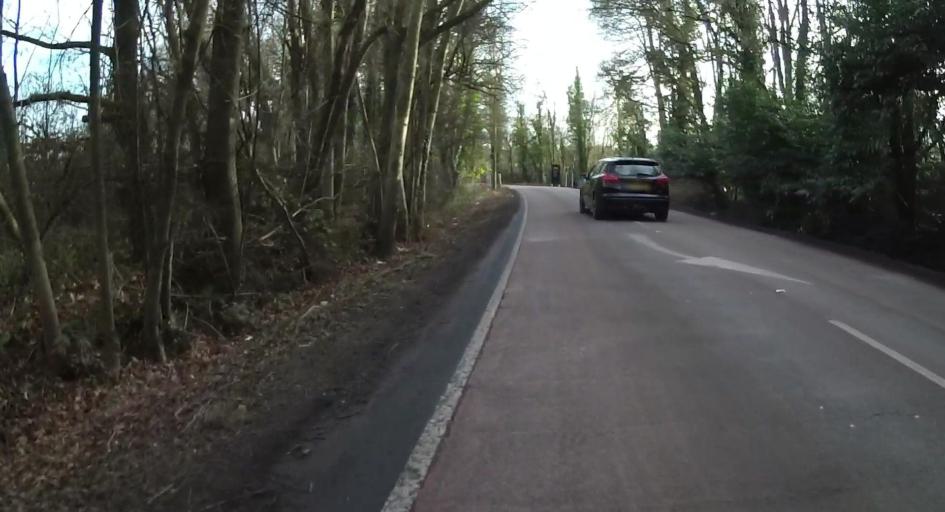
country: GB
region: England
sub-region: Wokingham
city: Wokingham
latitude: 51.3972
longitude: -0.8091
